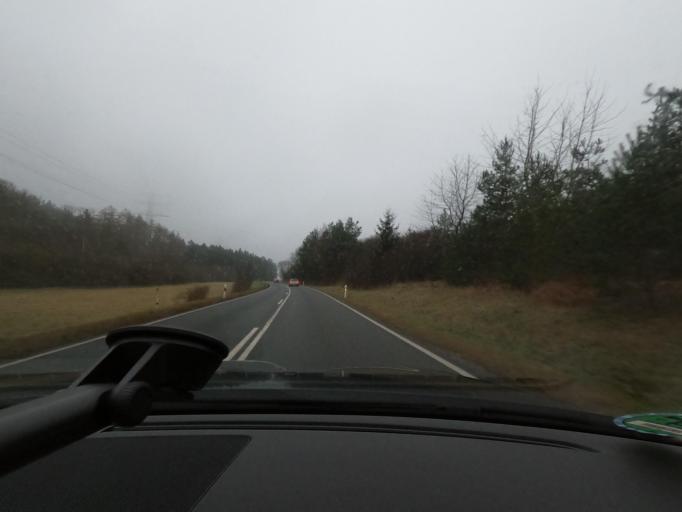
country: DE
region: Thuringia
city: Behringen
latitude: 50.7600
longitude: 11.0053
